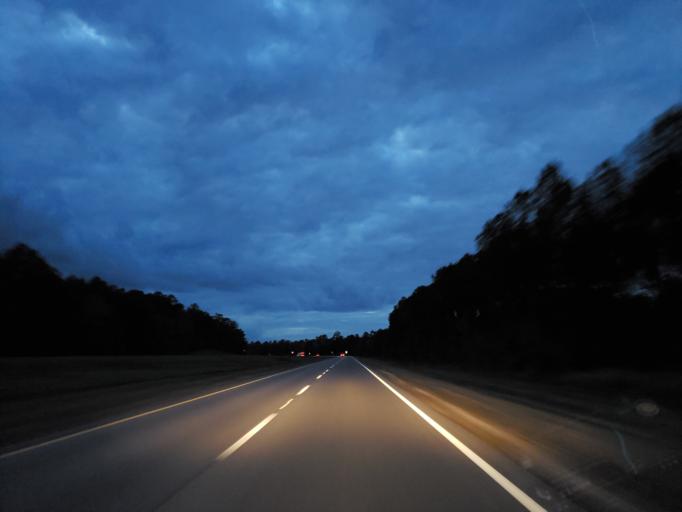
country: US
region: Mississippi
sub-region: Forrest County
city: Hattiesburg
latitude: 31.2446
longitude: -89.2314
